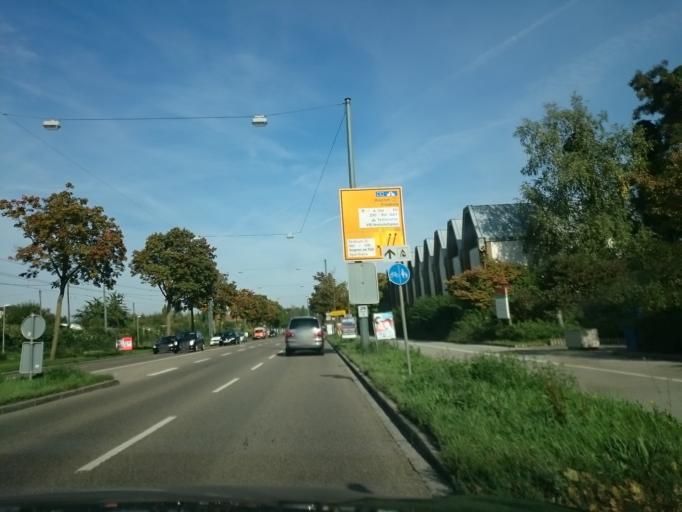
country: DE
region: Bavaria
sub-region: Swabia
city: Augsburg
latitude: 48.3491
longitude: 10.9040
